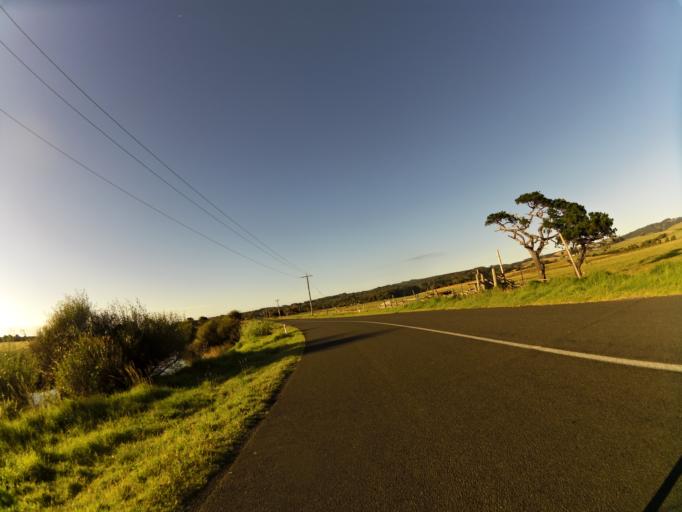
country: AU
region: Victoria
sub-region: Colac-Otway
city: Apollo Bay
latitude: -38.7623
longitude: 143.6618
